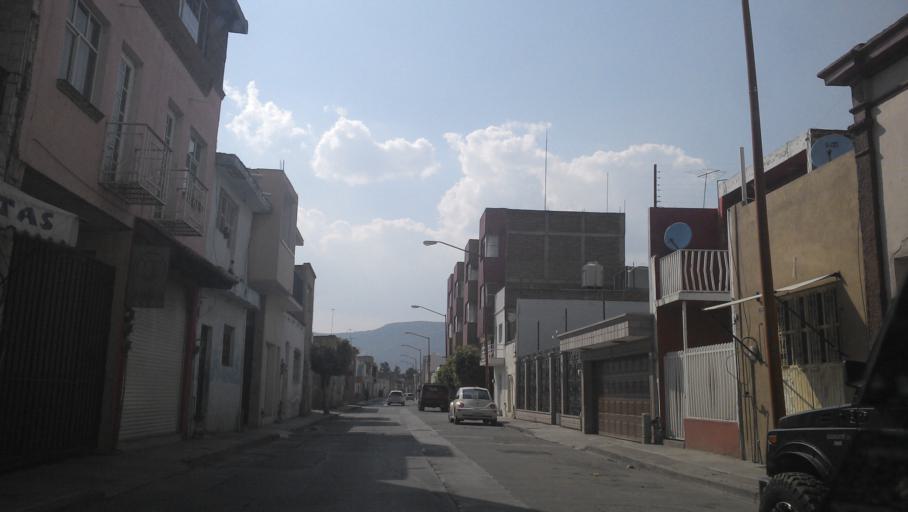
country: MX
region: Guanajuato
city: San Francisco del Rincon
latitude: 21.0216
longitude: -101.8581
